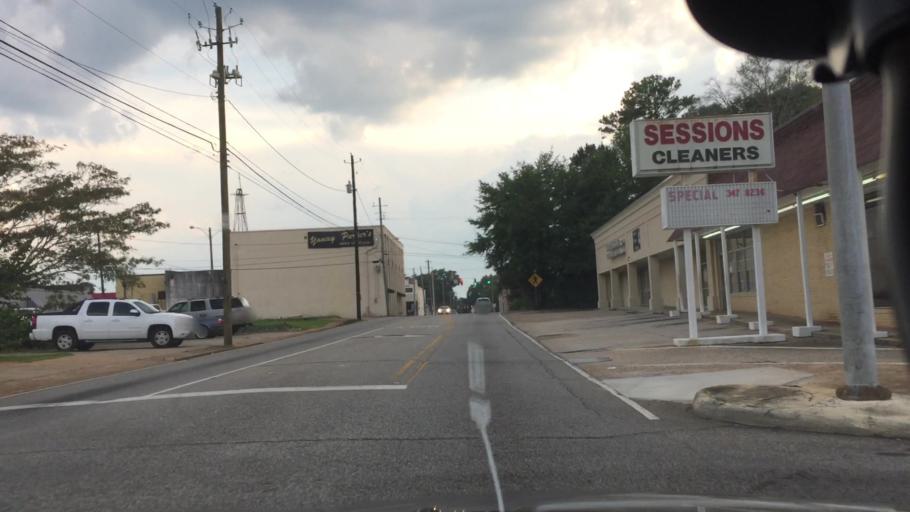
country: US
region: Alabama
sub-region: Coffee County
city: Enterprise
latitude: 31.3161
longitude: -85.8536
